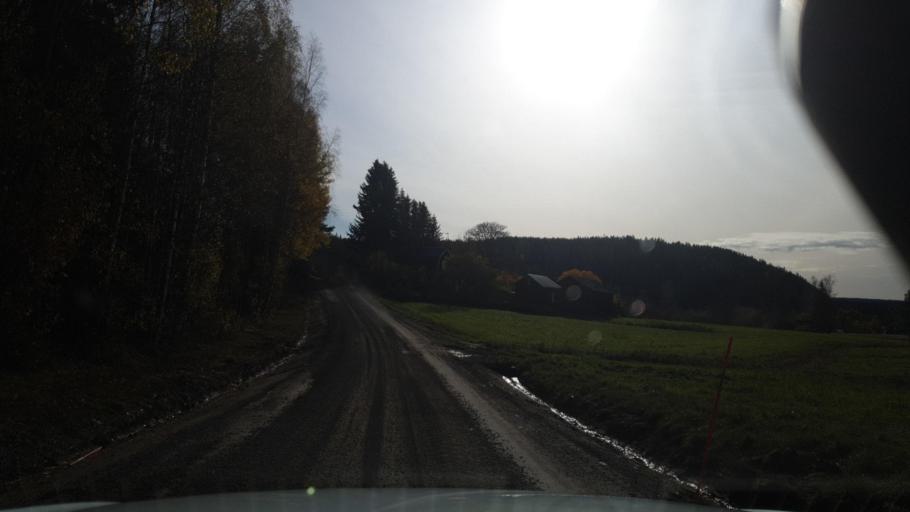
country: NO
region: Hedmark
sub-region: Eidskog
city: Skotterud
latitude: 59.7337
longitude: 12.0955
